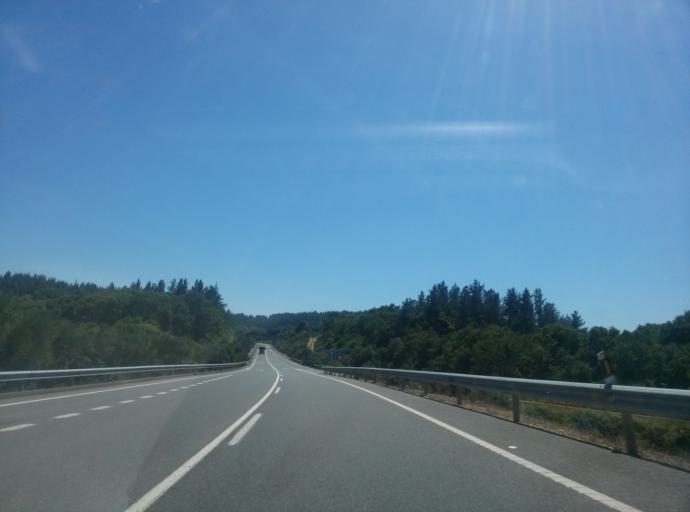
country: ES
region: Galicia
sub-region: Provincia de Lugo
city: Mos
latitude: 43.0983
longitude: -7.4747
